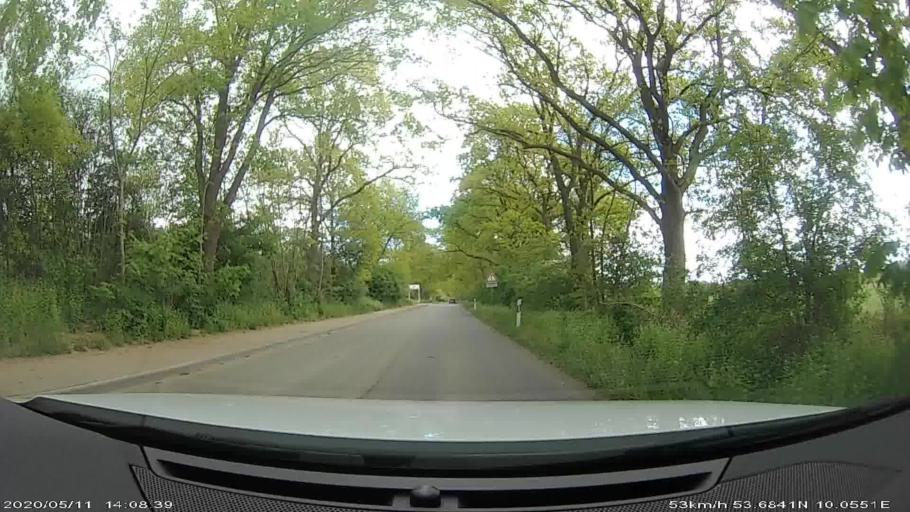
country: DE
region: Hamburg
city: Lemsahl-Mellingstedt
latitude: 53.6828
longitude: 10.0764
